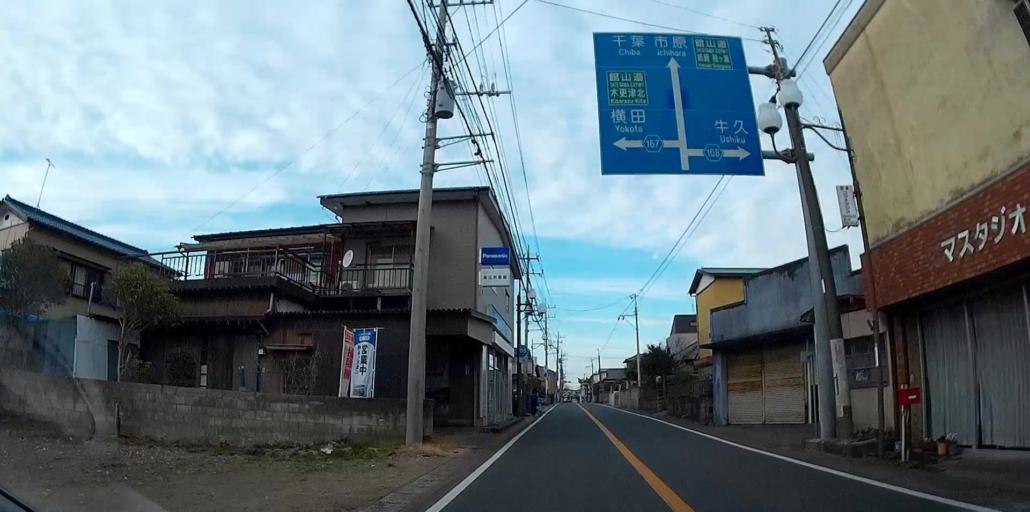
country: JP
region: Chiba
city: Kisarazu
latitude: 35.3653
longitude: 140.0587
